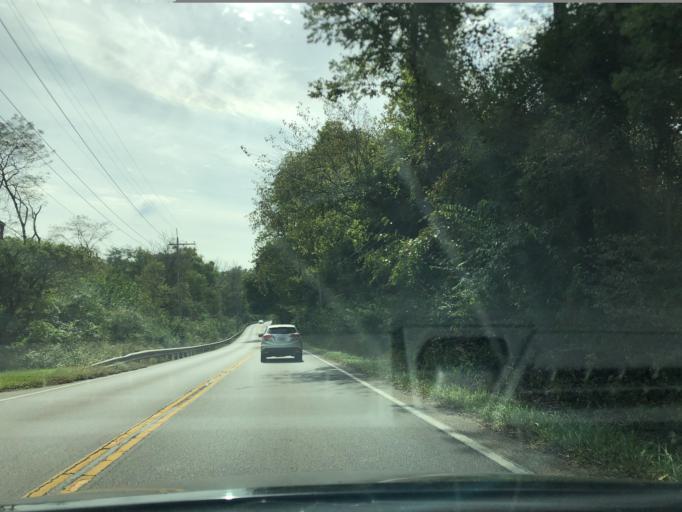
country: US
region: Ohio
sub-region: Clermont County
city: Milford
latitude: 39.1848
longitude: -84.2926
